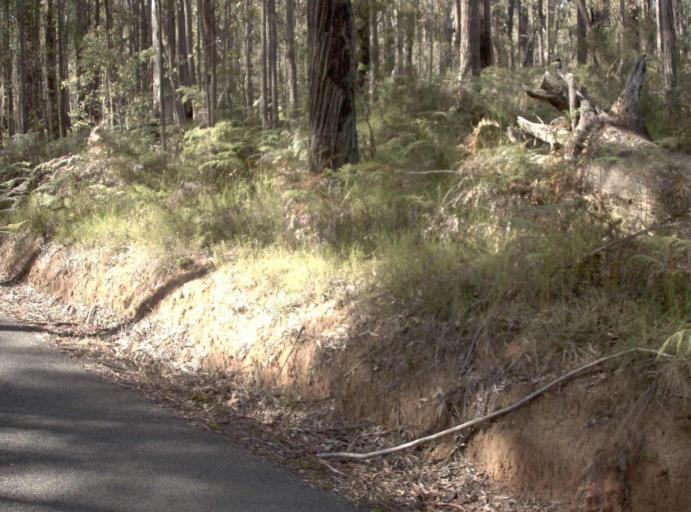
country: AU
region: New South Wales
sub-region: Bombala
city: Bombala
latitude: -37.3851
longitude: 148.6206
